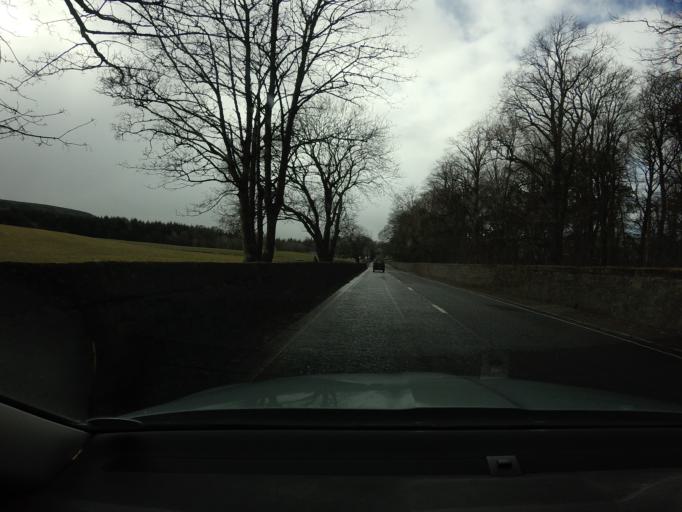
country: GB
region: Scotland
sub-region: South Lanarkshire
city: Douglas
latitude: 55.5600
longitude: -3.8358
